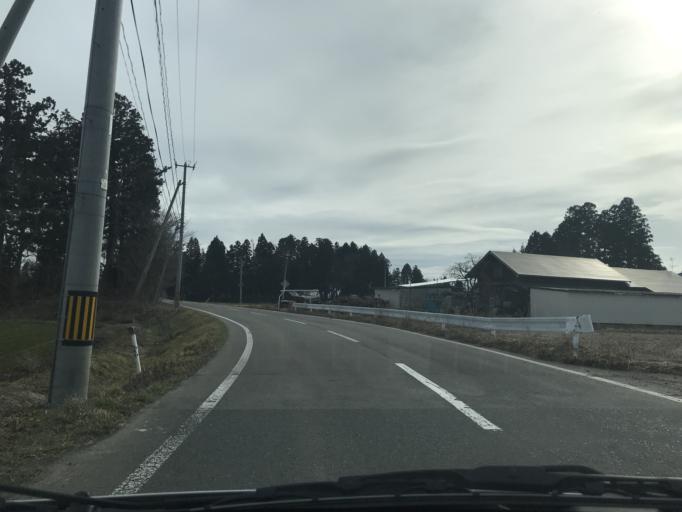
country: JP
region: Iwate
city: Hanamaki
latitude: 39.3509
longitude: 141.0599
